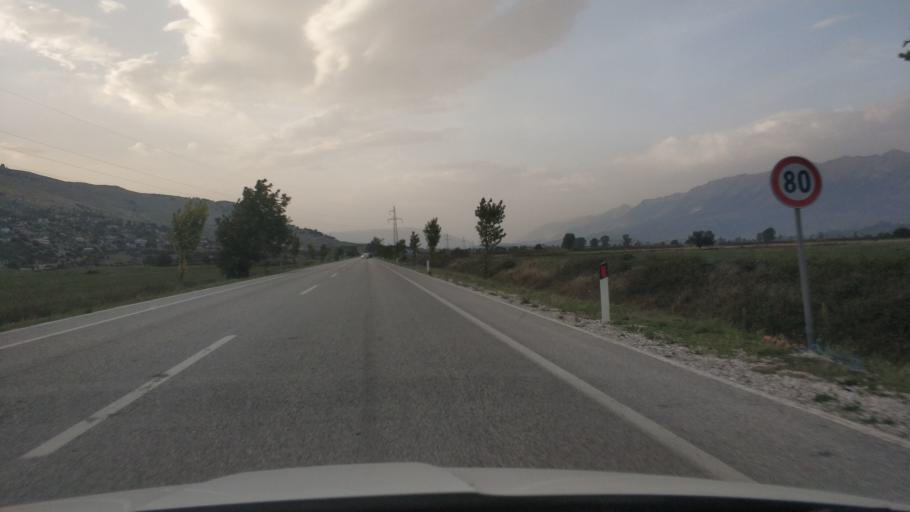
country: AL
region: Gjirokaster
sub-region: Rrethi i Gjirokastres
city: Libohove
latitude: 39.9585
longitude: 20.2473
